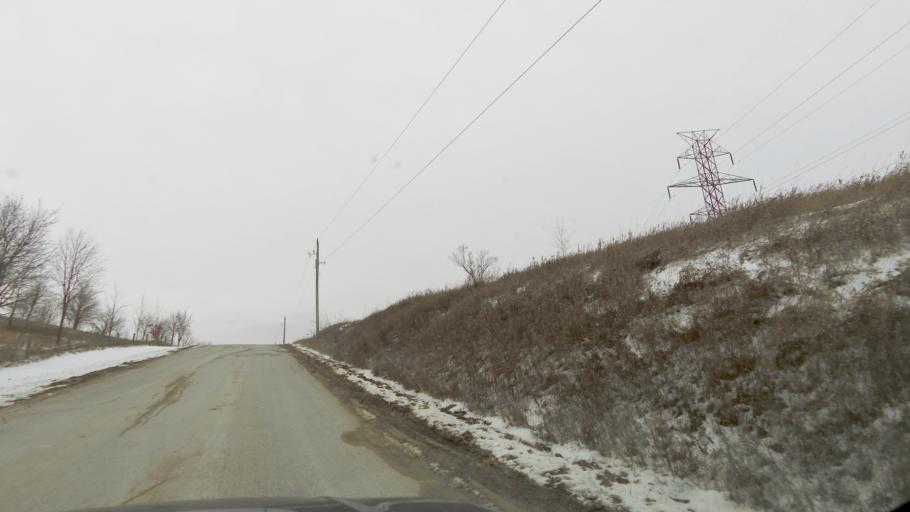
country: CA
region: Ontario
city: Vaughan
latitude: 43.9281
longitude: -79.6071
